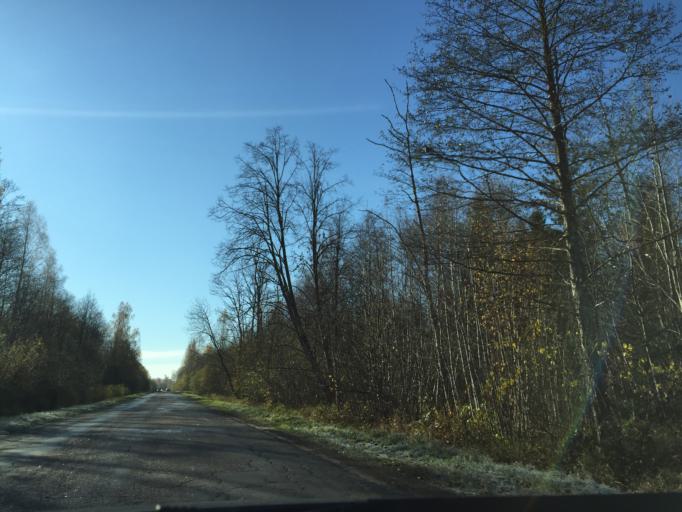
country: LV
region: Skriveri
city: Skriveri
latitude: 56.7191
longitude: 25.1583
